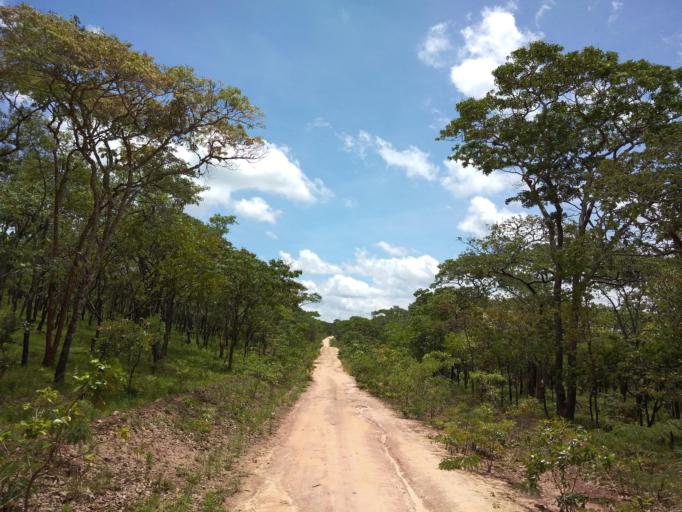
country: ZM
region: Central
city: Mkushi
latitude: -13.9257
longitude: 29.8645
